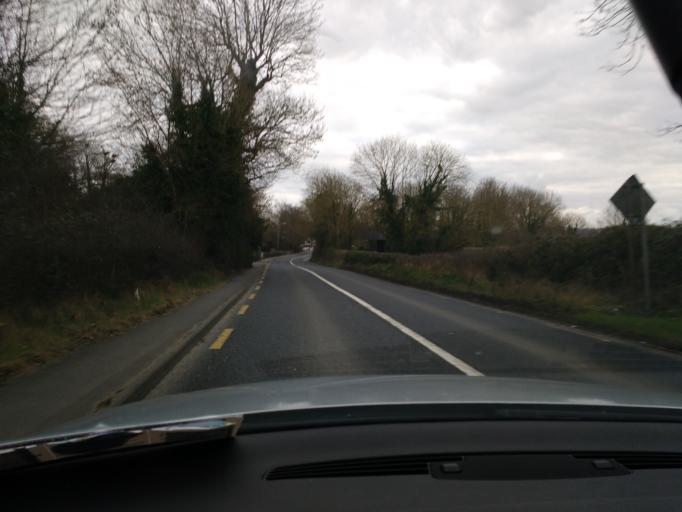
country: IE
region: Leinster
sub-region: Kilkenny
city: Kilkenny
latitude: 52.6759
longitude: -7.2733
